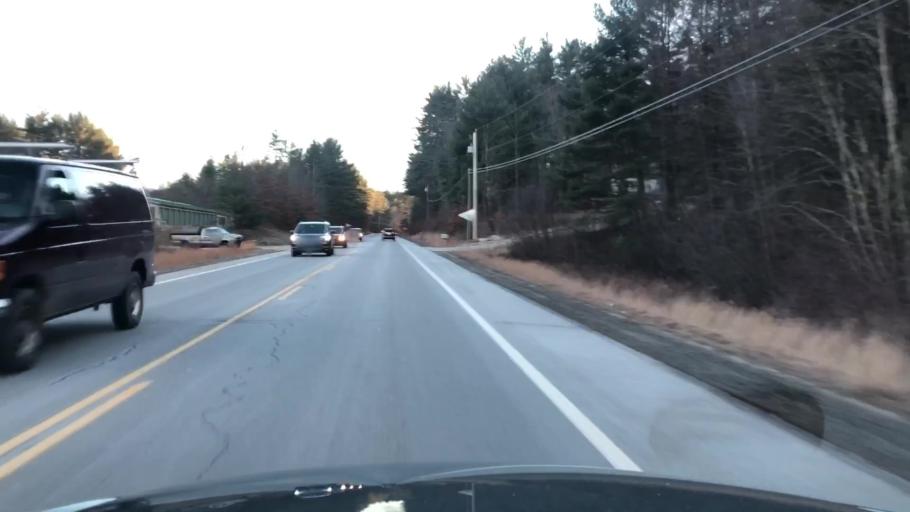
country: US
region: New Hampshire
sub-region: Hillsborough County
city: Brookline
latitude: 42.7209
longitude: -71.6625
